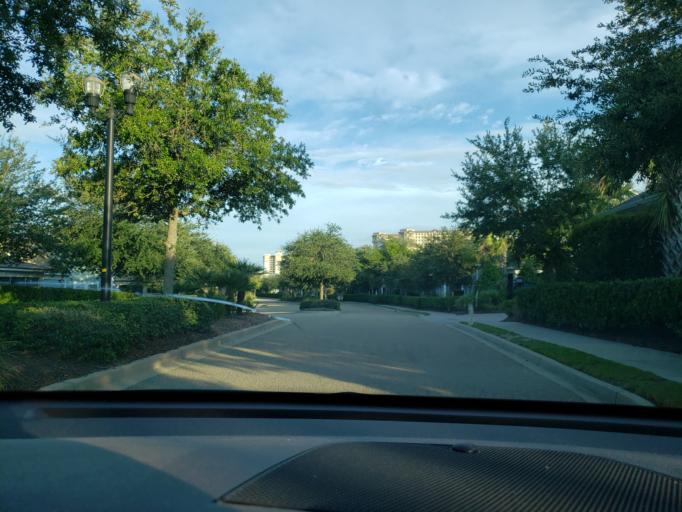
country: US
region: South Carolina
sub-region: Horry County
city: North Myrtle Beach
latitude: 33.7942
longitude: -78.7401
